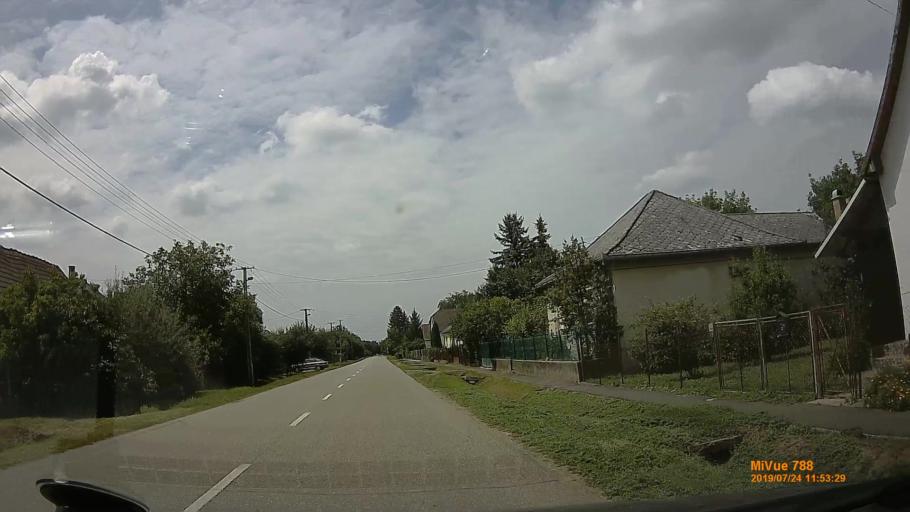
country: UA
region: Zakarpattia
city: Batiovo
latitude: 48.2267
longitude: 22.4224
